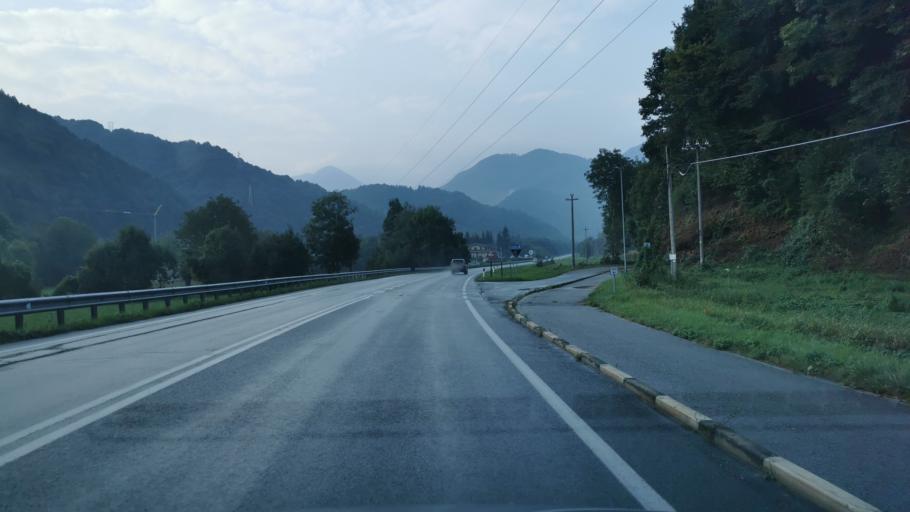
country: IT
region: Piedmont
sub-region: Provincia di Cuneo
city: Robilante
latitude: 44.2746
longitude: 7.5189
